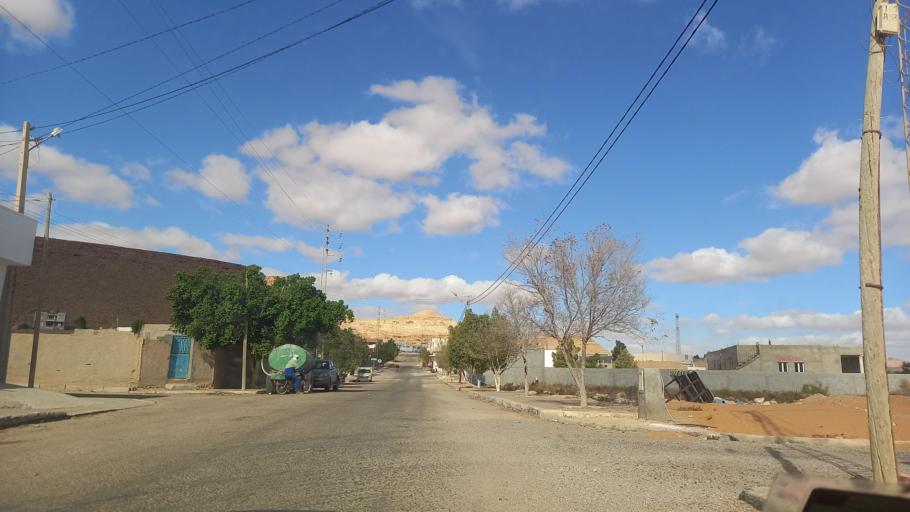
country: TN
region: Tataouine
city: Tataouine
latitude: 32.9811
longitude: 10.2668
